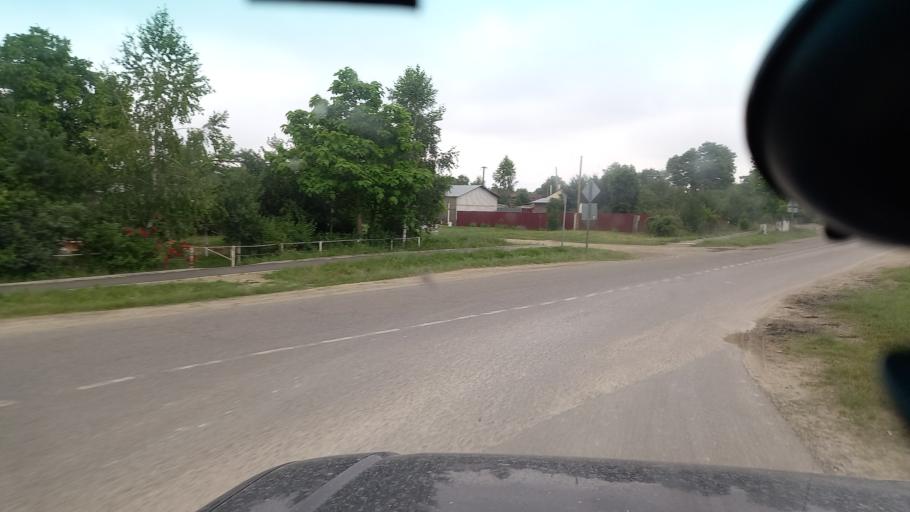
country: RU
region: Krasnodarskiy
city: Mostovskoy
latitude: 44.4232
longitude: 40.7748
